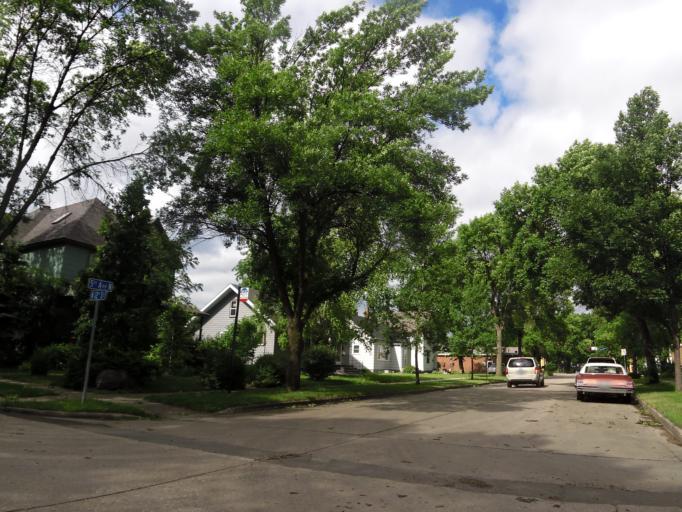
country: US
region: North Dakota
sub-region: Grand Forks County
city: Grand Forks
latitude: 47.9244
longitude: -97.0436
